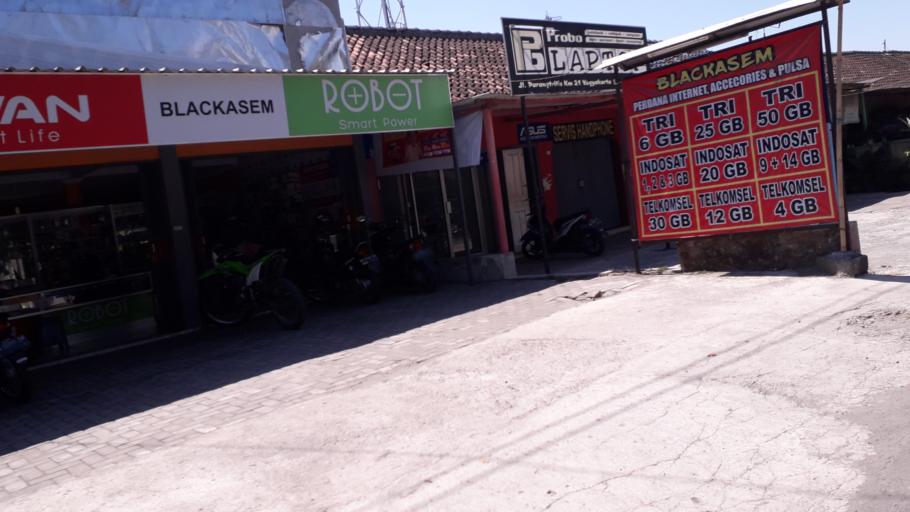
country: ID
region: Daerah Istimewa Yogyakarta
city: Pundong
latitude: -7.9739
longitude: 110.3184
